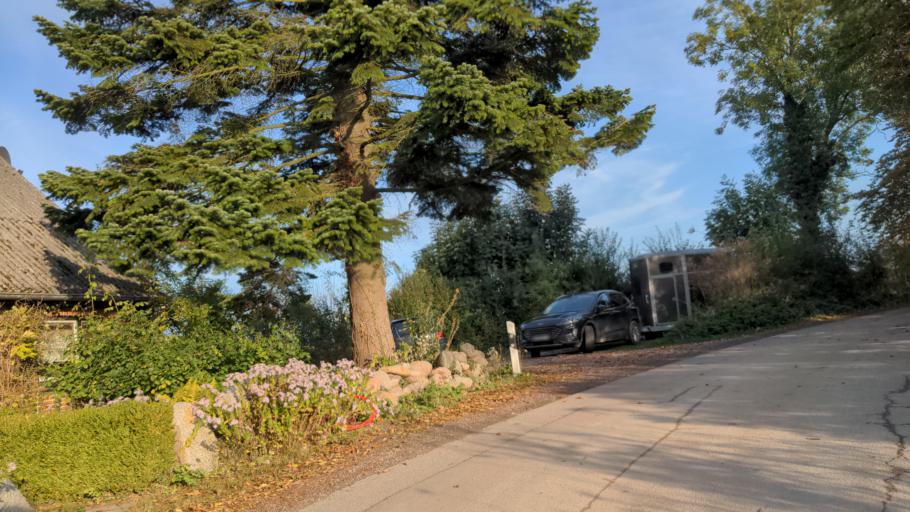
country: DE
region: Schleswig-Holstein
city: Manhagen
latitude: 54.1875
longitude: 10.9432
